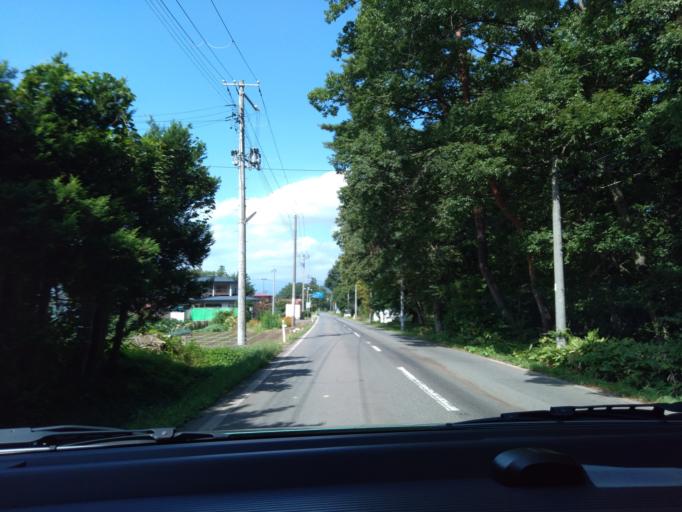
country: JP
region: Iwate
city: Shizukuishi
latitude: 39.6571
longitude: 140.9923
